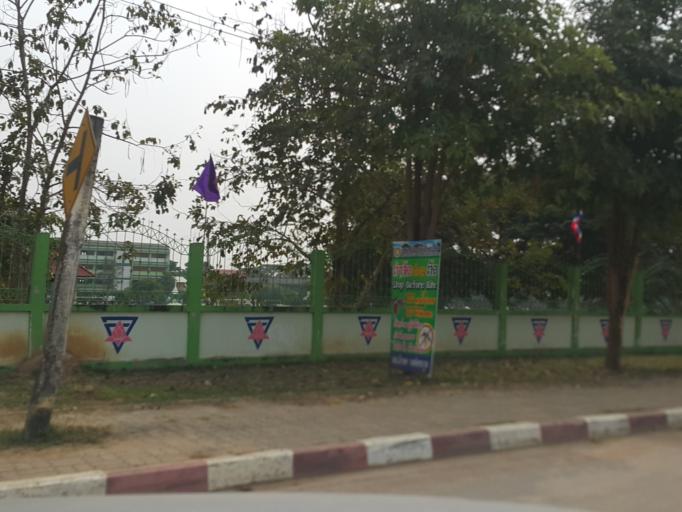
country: TH
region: Lampang
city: Ko Kha
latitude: 18.1953
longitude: 99.4018
